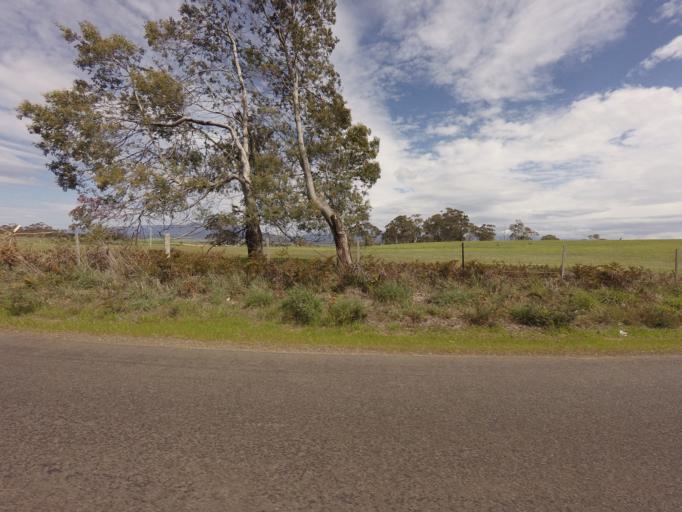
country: AU
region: Tasmania
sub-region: Northern Midlands
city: Longford
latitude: -41.7700
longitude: 147.2173
